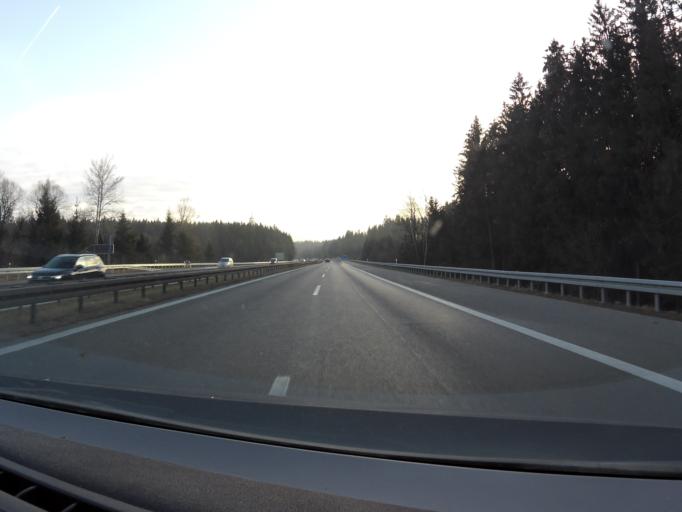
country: DE
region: Bavaria
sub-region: Upper Bavaria
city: Wolfratshausen
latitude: 47.9006
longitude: 11.3970
